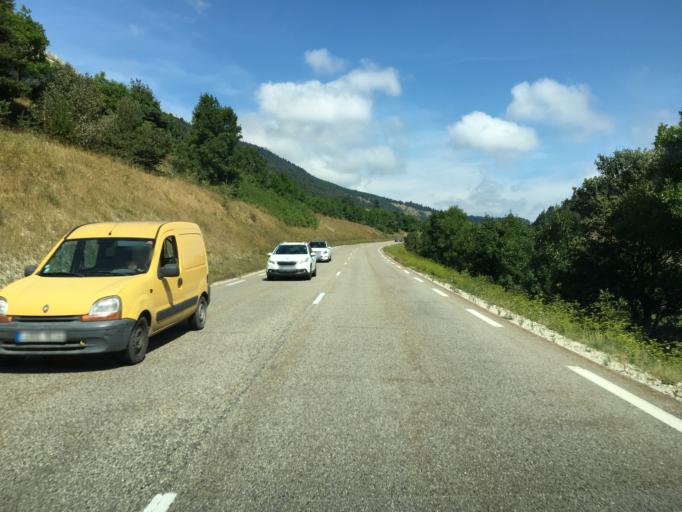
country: FR
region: Rhone-Alpes
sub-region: Departement de l'Isere
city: Mens
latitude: 44.7075
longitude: 5.6778
